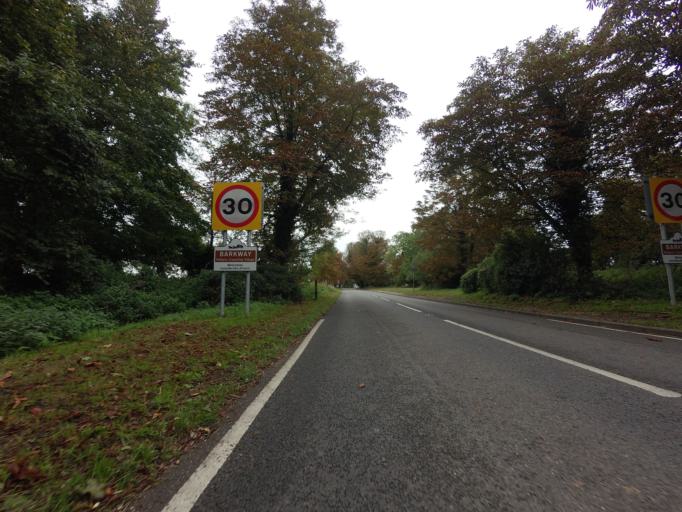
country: GB
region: England
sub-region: Hertfordshire
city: Reed
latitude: 52.0066
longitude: 0.0192
